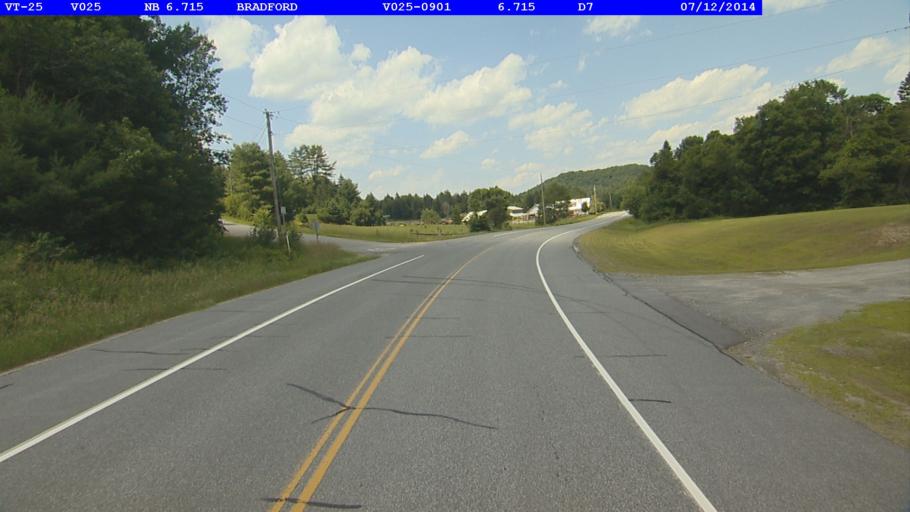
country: US
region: New Hampshire
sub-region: Grafton County
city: Haverhill
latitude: 44.0383
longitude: -72.1995
